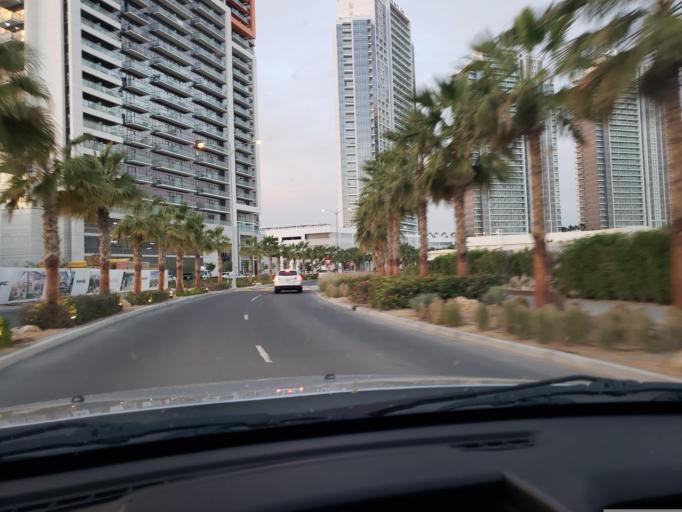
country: AE
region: Dubai
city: Dubai
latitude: 25.0221
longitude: 55.2434
